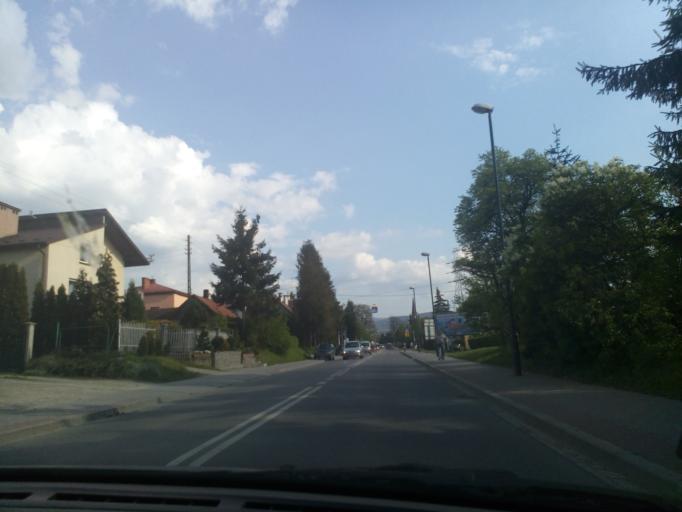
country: PL
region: Lesser Poland Voivodeship
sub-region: Powiat nowosadecki
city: Nawojowa
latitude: 49.5866
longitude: 20.7252
